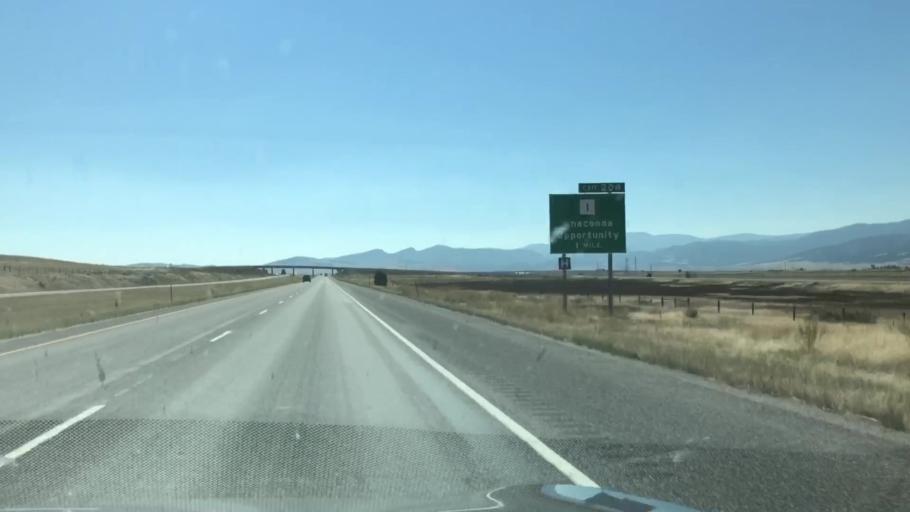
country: US
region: Montana
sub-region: Deer Lodge County
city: Warm Springs
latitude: 46.1131
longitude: -112.8004
